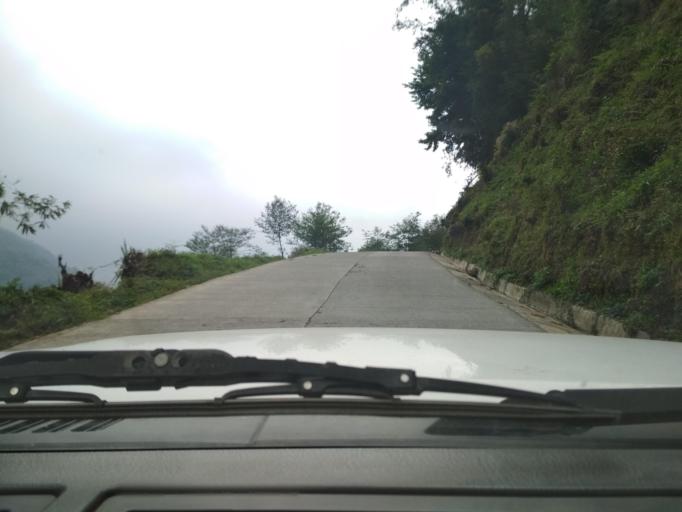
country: MX
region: Veracruz
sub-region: La Perla
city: Barrio de San Miguel
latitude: 18.9348
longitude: -97.1265
